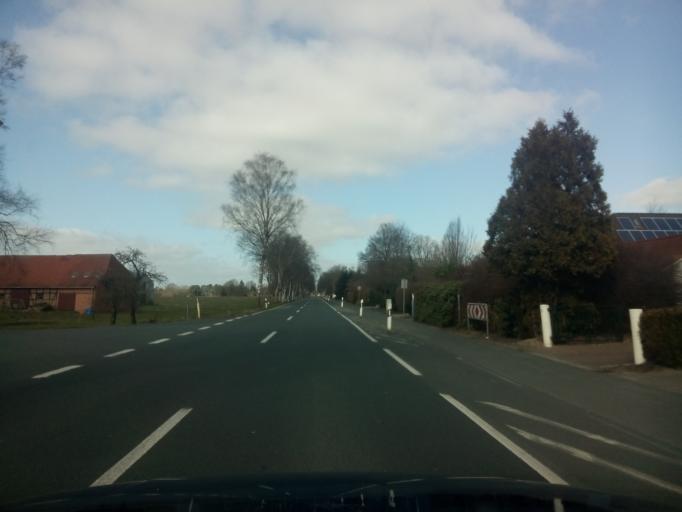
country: DE
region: Lower Saxony
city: Grasberg
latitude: 53.1965
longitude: 8.9764
